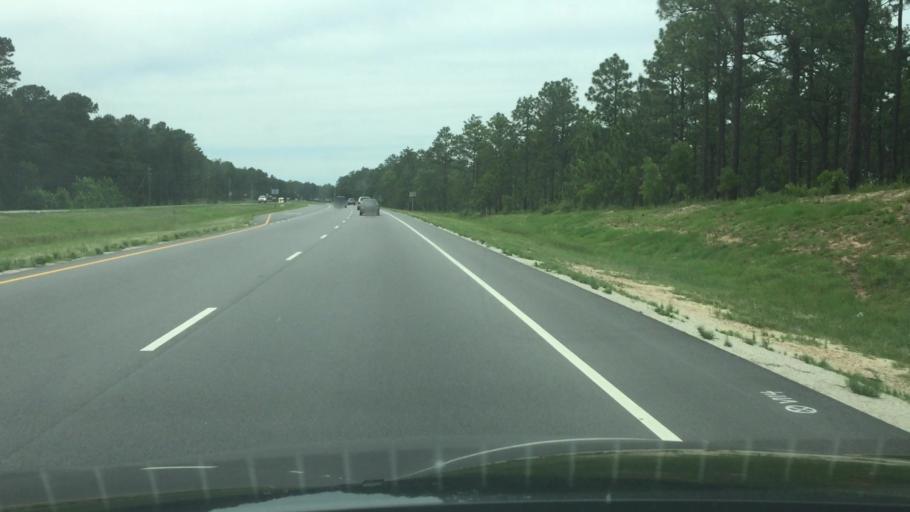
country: US
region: North Carolina
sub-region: Cumberland County
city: Spring Lake
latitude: 35.2267
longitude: -79.0107
